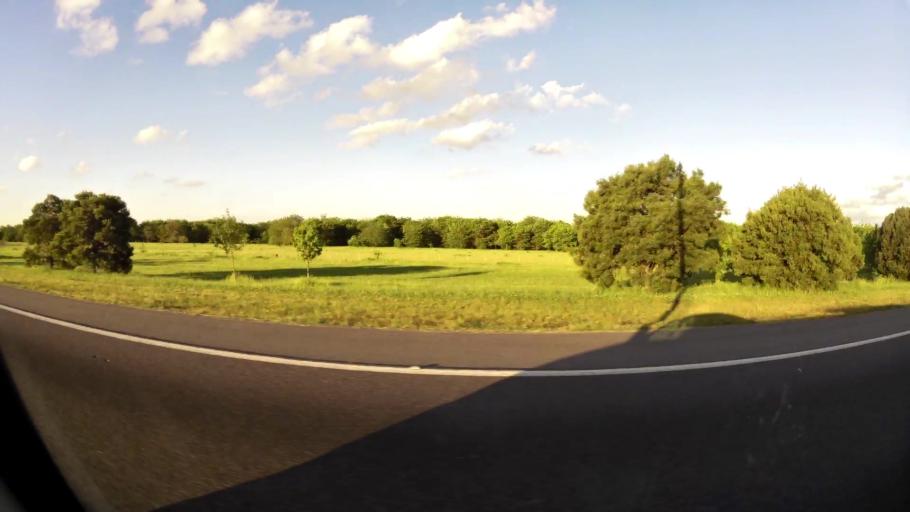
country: AR
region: Buenos Aires
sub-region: Partido de Quilmes
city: Quilmes
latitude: -34.8147
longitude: -58.1112
